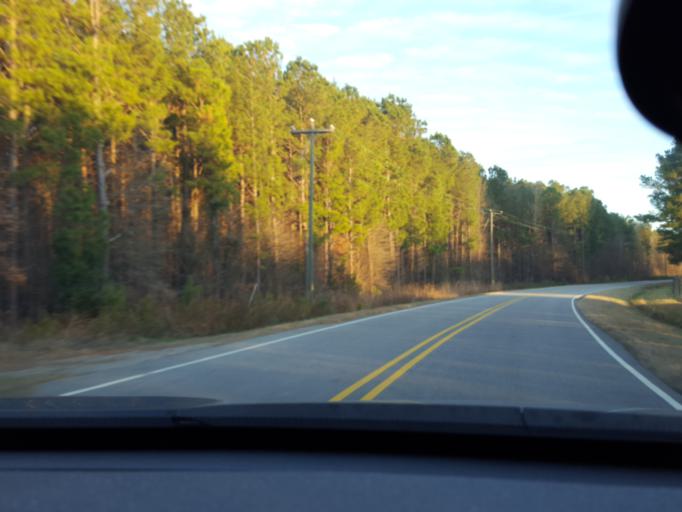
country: US
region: North Carolina
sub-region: Hertford County
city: Ahoskie
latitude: 36.2614
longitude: -77.1318
